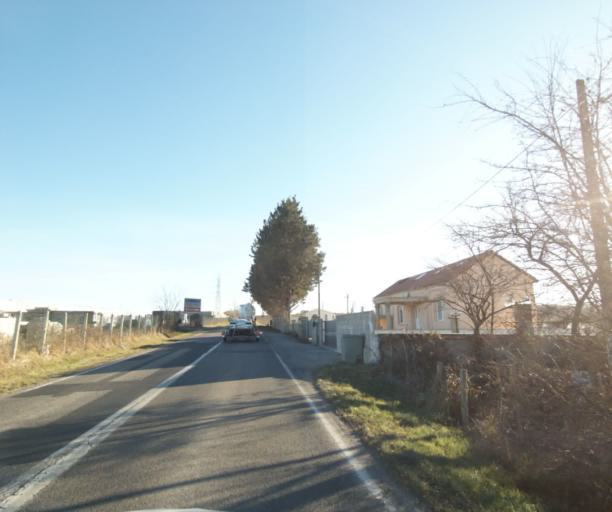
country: FR
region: Lorraine
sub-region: Departement de Meurthe-et-Moselle
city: Art-sur-Meurthe
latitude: 48.6381
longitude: 6.2540
